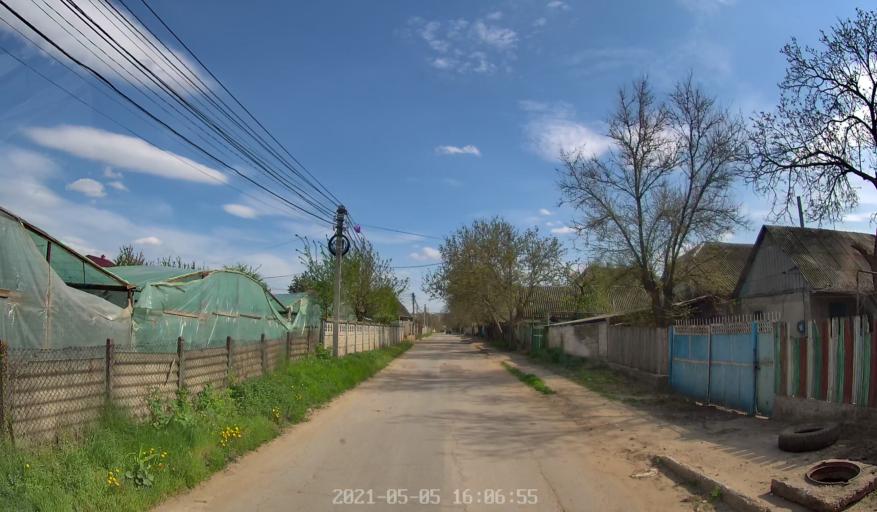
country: MD
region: Criuleni
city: Criuleni
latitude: 47.1437
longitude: 29.2000
